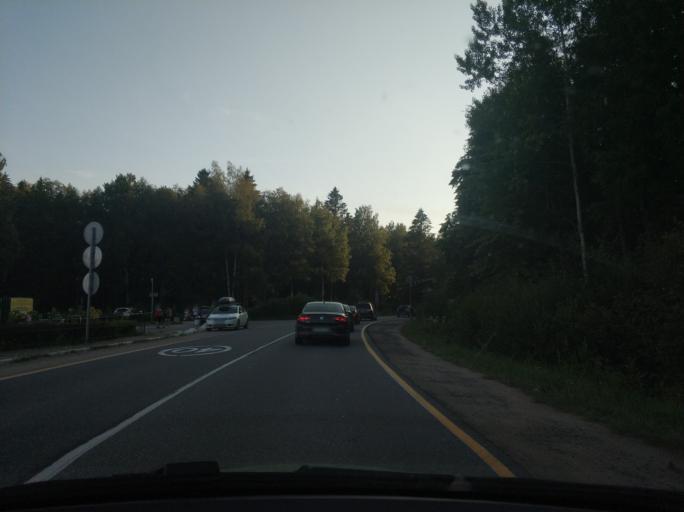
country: RU
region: Leningrad
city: Borisova Griva
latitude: 60.0818
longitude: 31.0666
